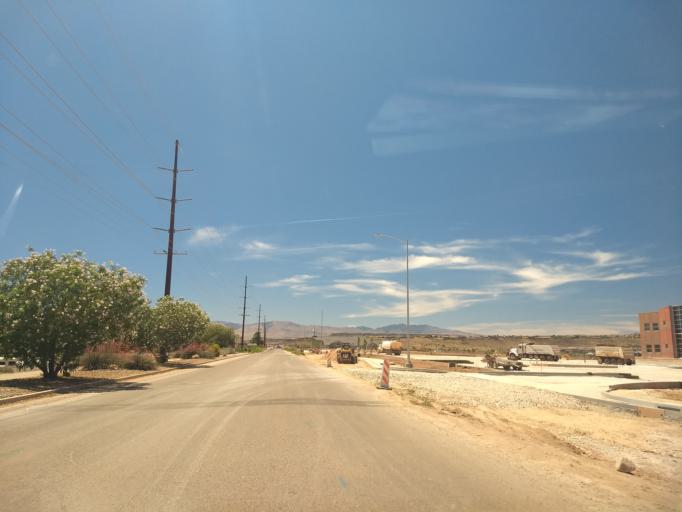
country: US
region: Utah
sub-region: Washington County
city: Washington
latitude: 37.0888
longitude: -113.5141
